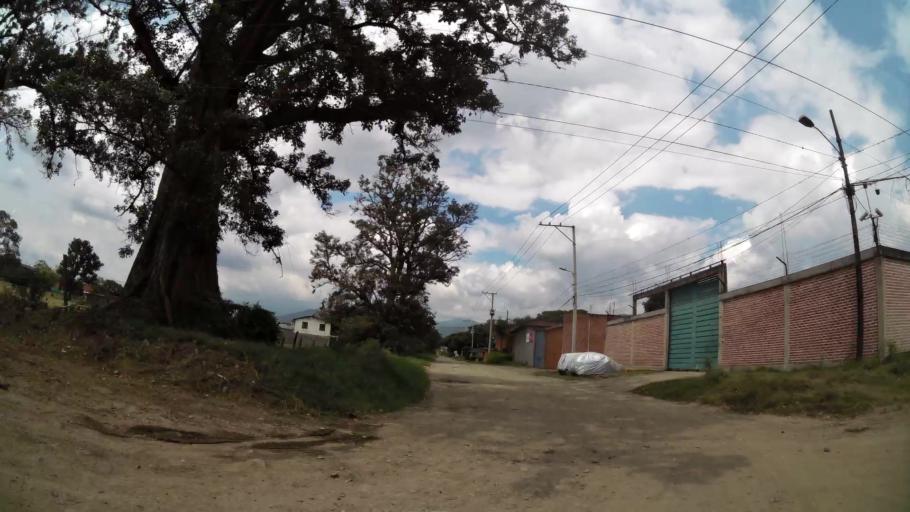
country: CO
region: Valle del Cauca
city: Cali
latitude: 3.4974
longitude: -76.4788
